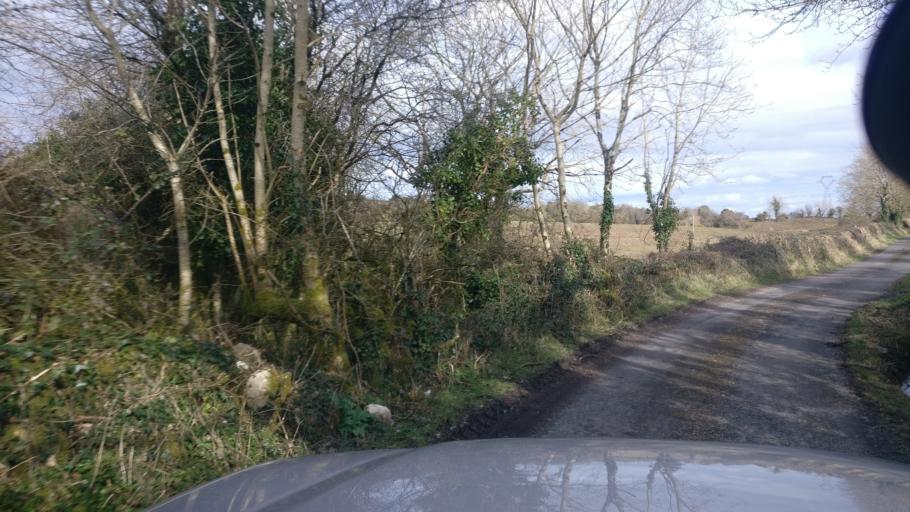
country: IE
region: Connaught
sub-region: County Galway
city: Loughrea
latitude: 53.1896
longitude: -8.4978
